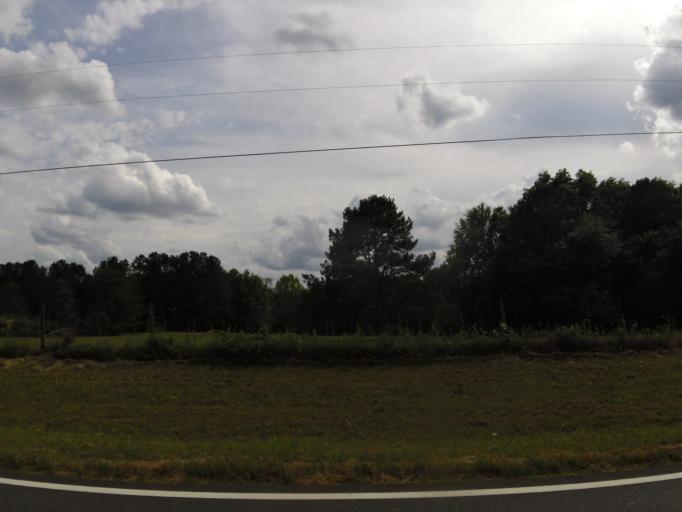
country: US
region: Georgia
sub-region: McDuffie County
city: Thomson
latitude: 33.5258
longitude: -82.4708
